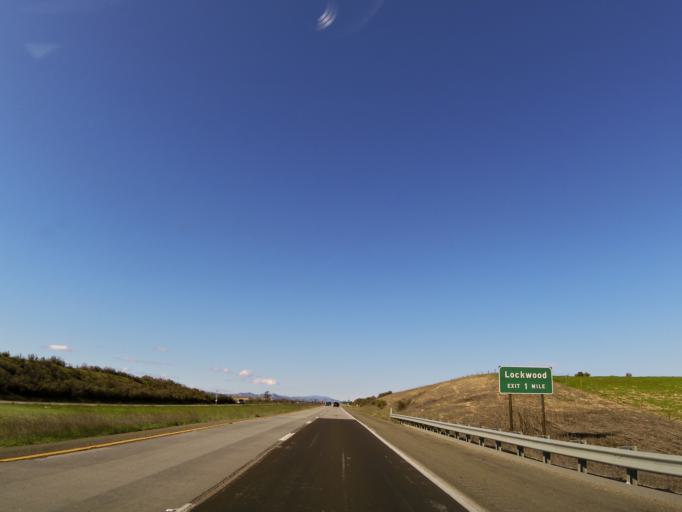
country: US
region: California
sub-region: Monterey County
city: King City
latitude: 36.0833
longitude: -121.0066
